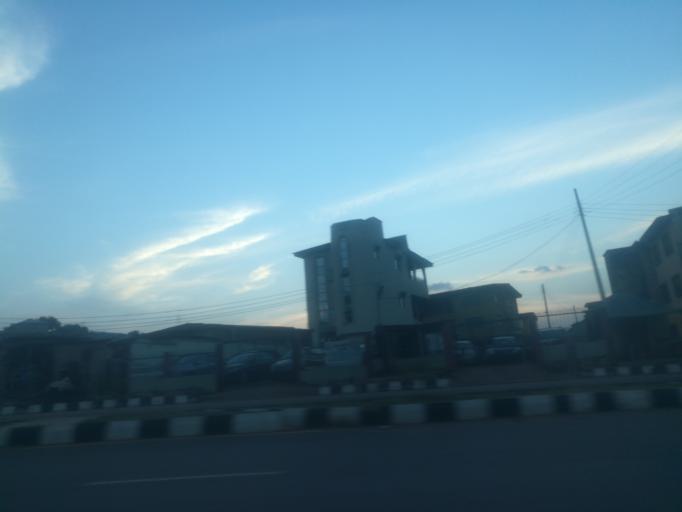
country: NG
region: Ogun
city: Abeokuta
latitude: 7.1705
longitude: 3.3712
